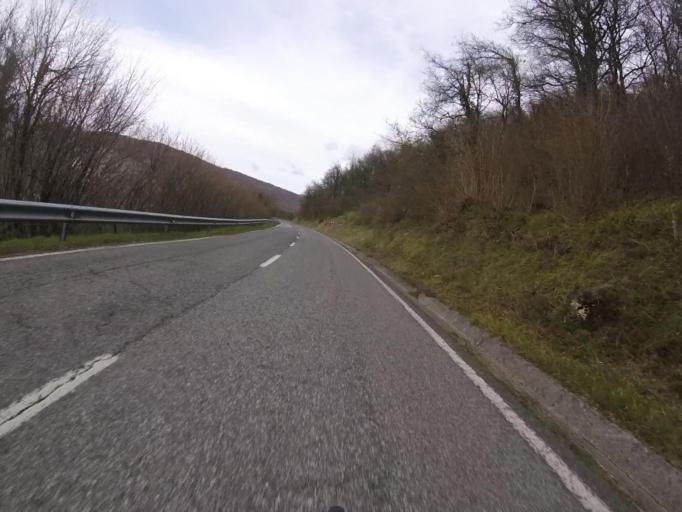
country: ES
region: Navarre
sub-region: Provincia de Navarra
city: Olazagutia
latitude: 42.8727
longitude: -2.1828
